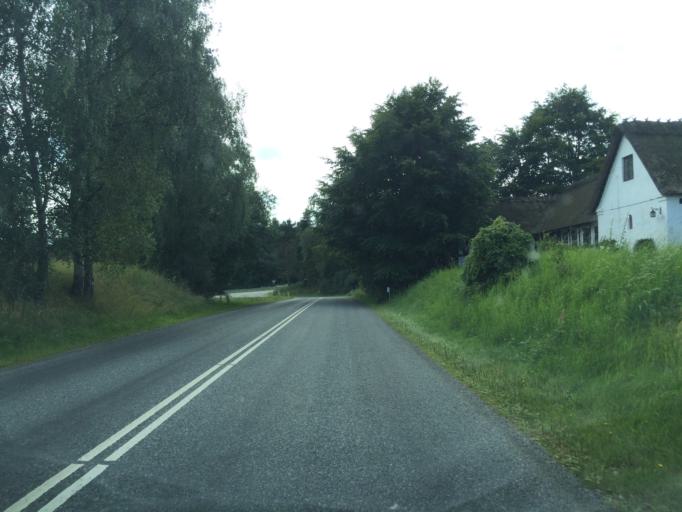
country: DK
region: South Denmark
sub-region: Faaborg-Midtfyn Kommune
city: Faaborg
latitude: 55.1498
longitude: 10.2649
